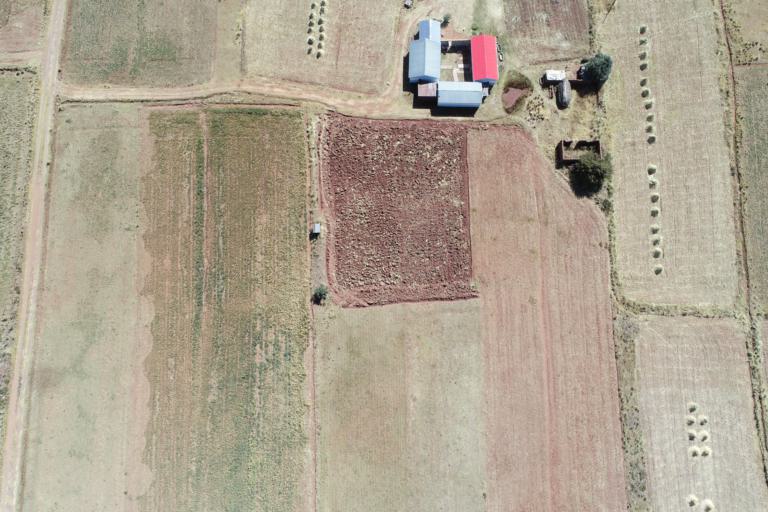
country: BO
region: La Paz
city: Tiahuanaco
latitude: -16.6020
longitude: -68.7810
